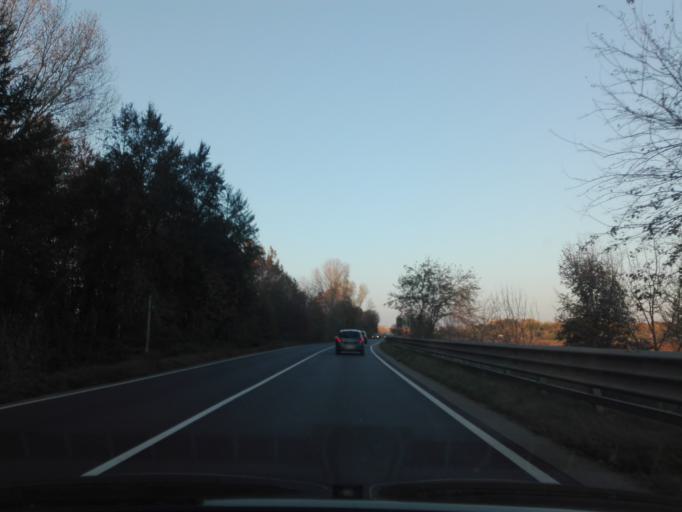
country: IT
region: Lombardy
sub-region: Provincia di Mantova
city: Cerese
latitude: 45.1337
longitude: 10.7904
